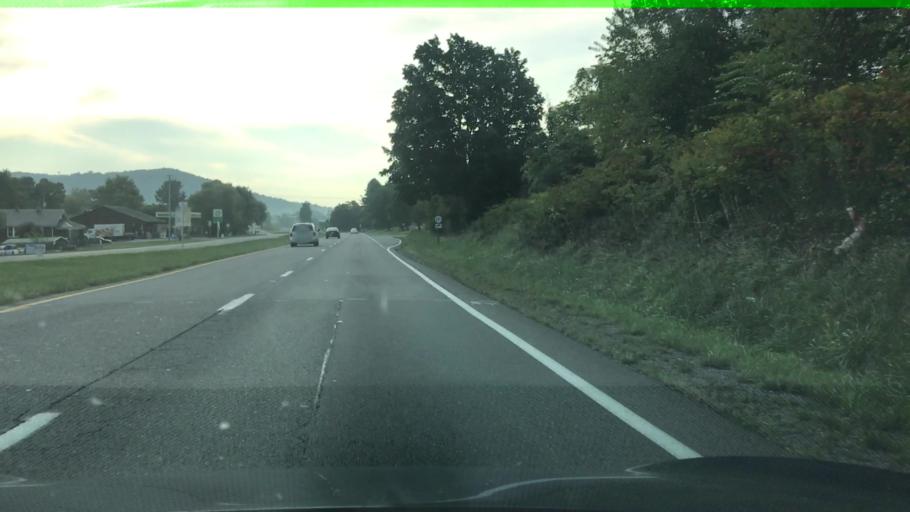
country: US
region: Virginia
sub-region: Botetourt County
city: Blue Ridge
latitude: 37.3805
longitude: -79.7220
